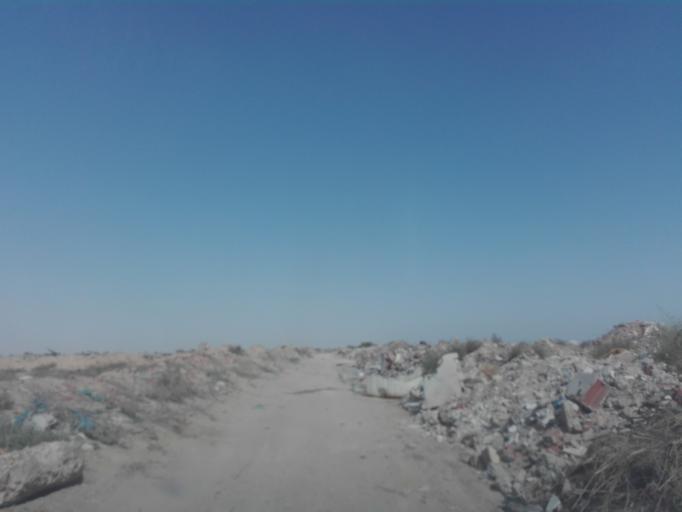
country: TN
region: Qabis
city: Gabes
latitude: 33.9604
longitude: 10.0669
